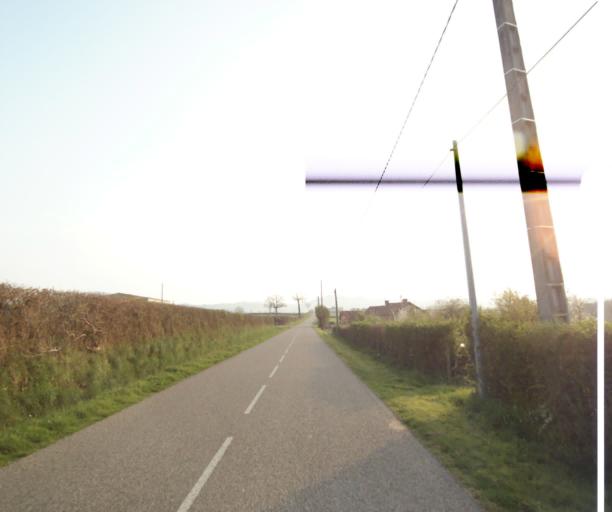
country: FR
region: Bourgogne
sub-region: Departement de Saone-et-Loire
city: Charolles
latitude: 46.4416
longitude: 4.4238
